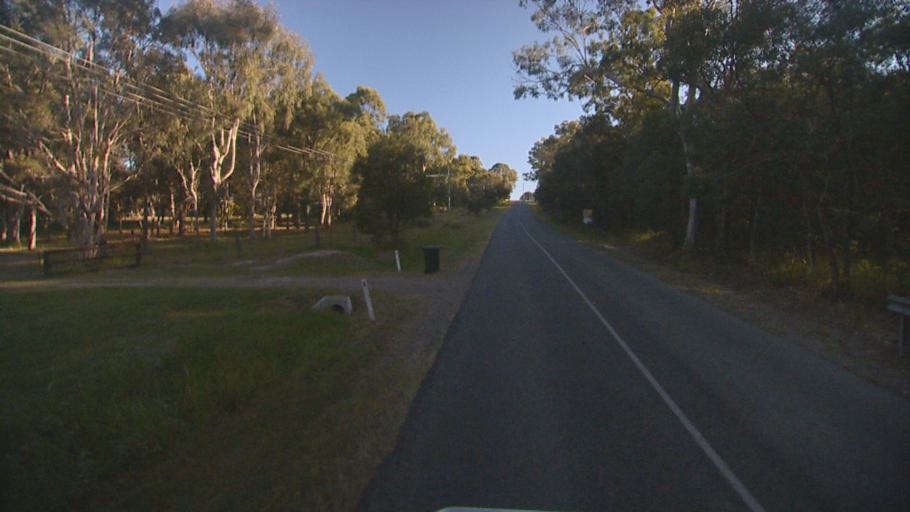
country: AU
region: Queensland
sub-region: Logan
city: Logan Reserve
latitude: -27.7227
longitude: 153.1074
